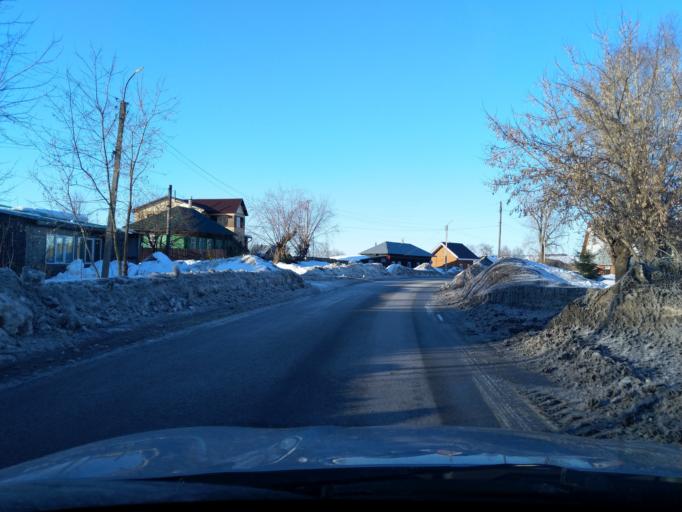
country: RU
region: Perm
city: Polazna
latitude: 58.2966
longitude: 56.4158
